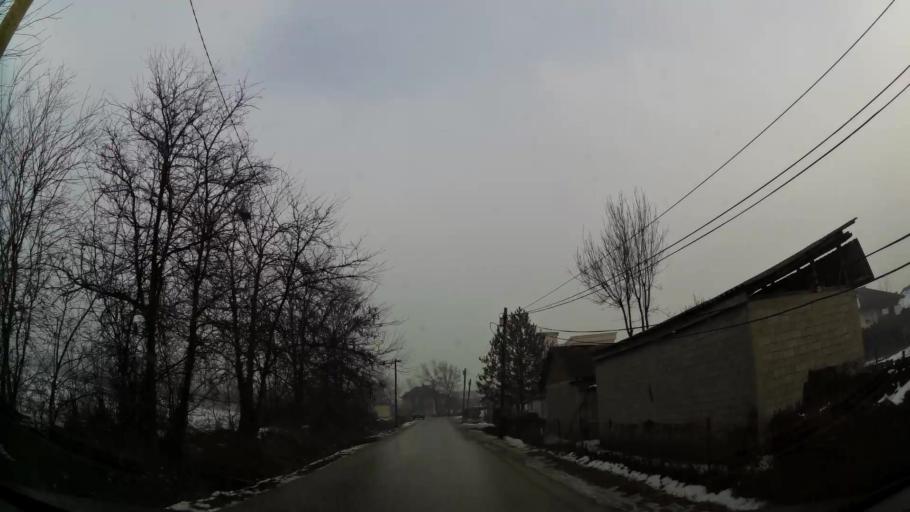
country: MK
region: Ilinden
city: Idrizovo
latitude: 41.9576
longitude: 21.5719
